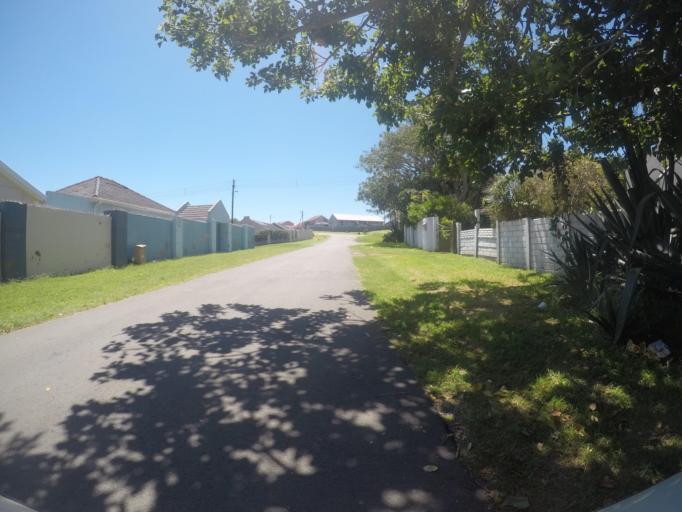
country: ZA
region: Eastern Cape
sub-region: Buffalo City Metropolitan Municipality
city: East London
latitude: -32.9565
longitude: 27.9963
